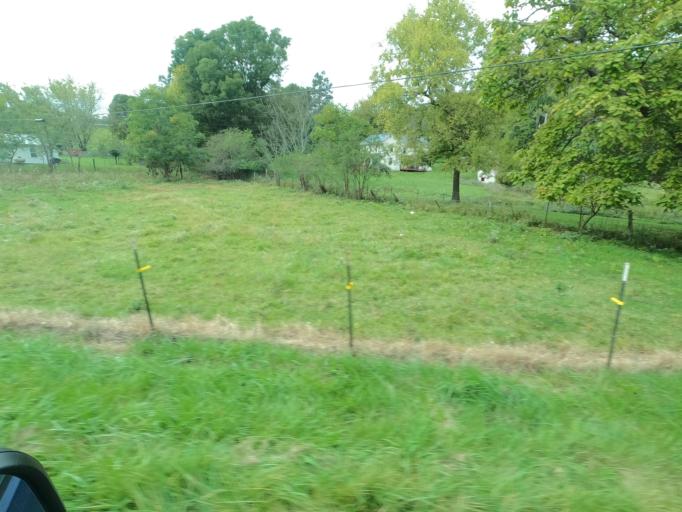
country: US
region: Tennessee
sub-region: Washington County
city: Jonesborough
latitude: 36.2629
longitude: -82.5350
